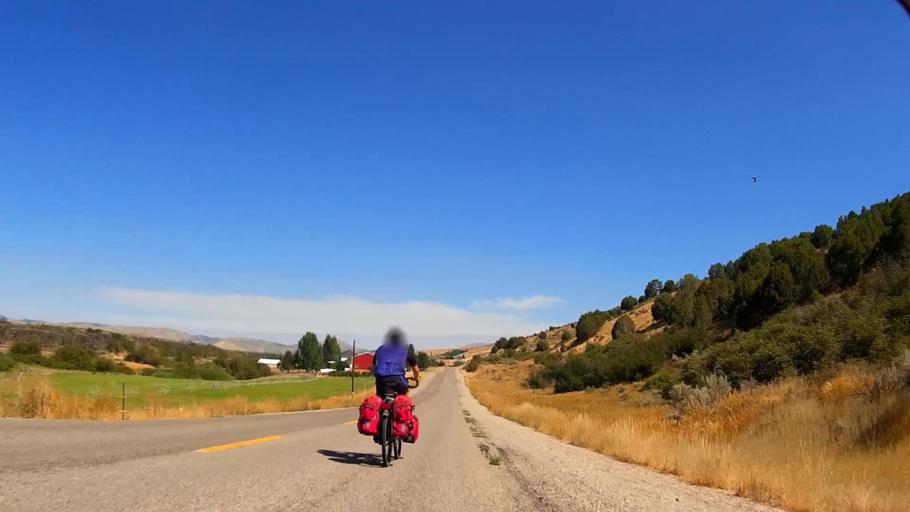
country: US
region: Idaho
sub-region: Bannock County
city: Pocatello
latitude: 42.7138
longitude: -112.2077
